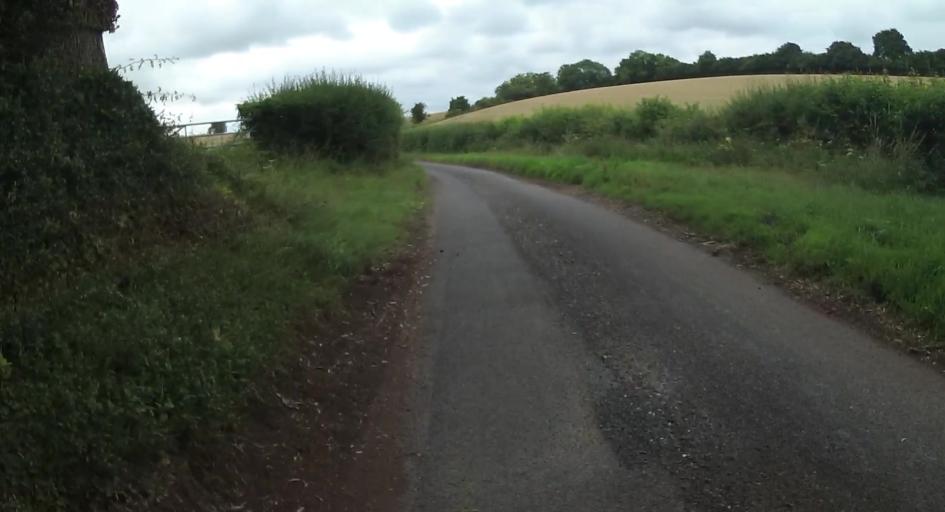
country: GB
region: England
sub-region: Hampshire
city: Four Marks
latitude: 51.0751
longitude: -1.1413
